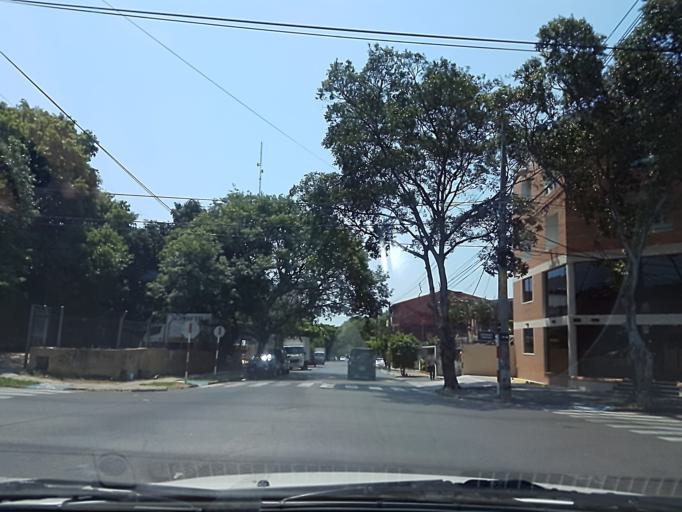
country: PY
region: Asuncion
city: Asuncion
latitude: -25.3014
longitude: -57.6093
